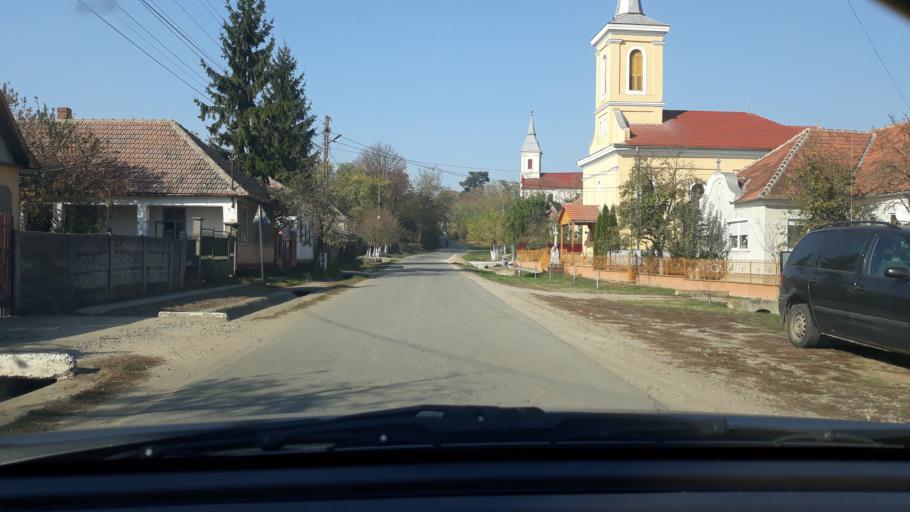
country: RO
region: Bihor
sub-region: Comuna Tarcea
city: Galospetreu
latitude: 47.4808
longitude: 22.2179
